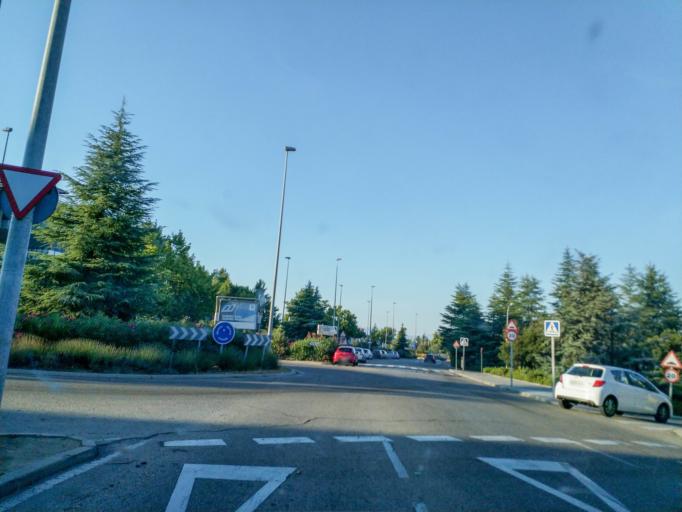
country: ES
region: Madrid
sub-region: Provincia de Madrid
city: Pozuelo de Alarcon
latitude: 40.4627
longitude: -3.8095
